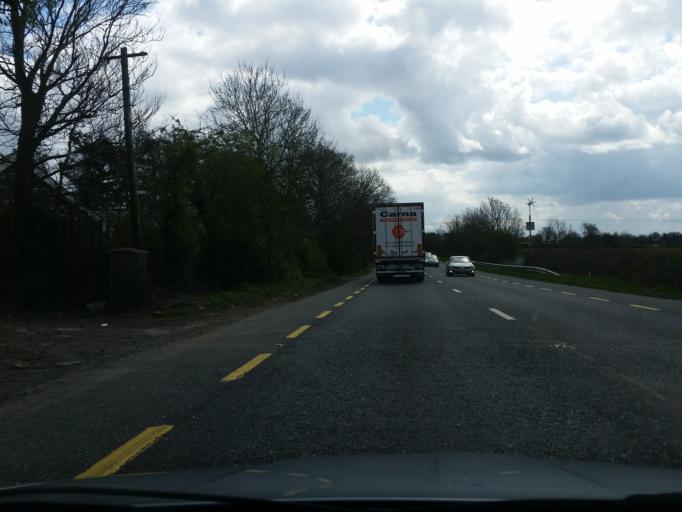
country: IE
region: Leinster
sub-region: An Mhi
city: Ashbourne
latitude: 53.5424
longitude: -6.4286
